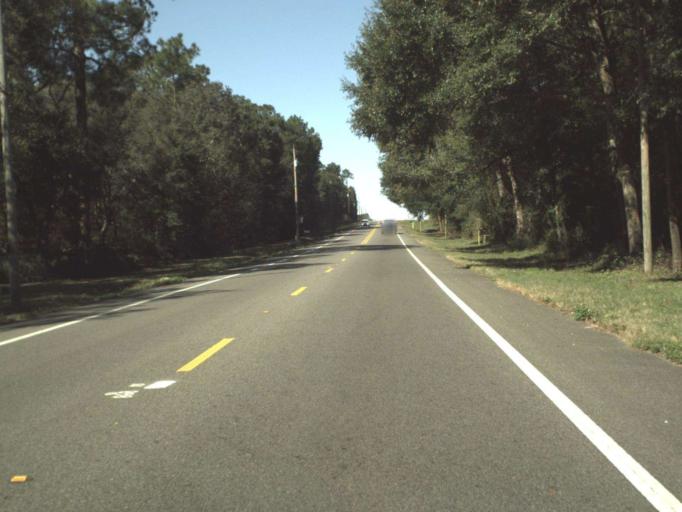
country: US
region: Florida
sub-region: Santa Rosa County
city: East Milton
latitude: 30.5892
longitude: -86.9354
